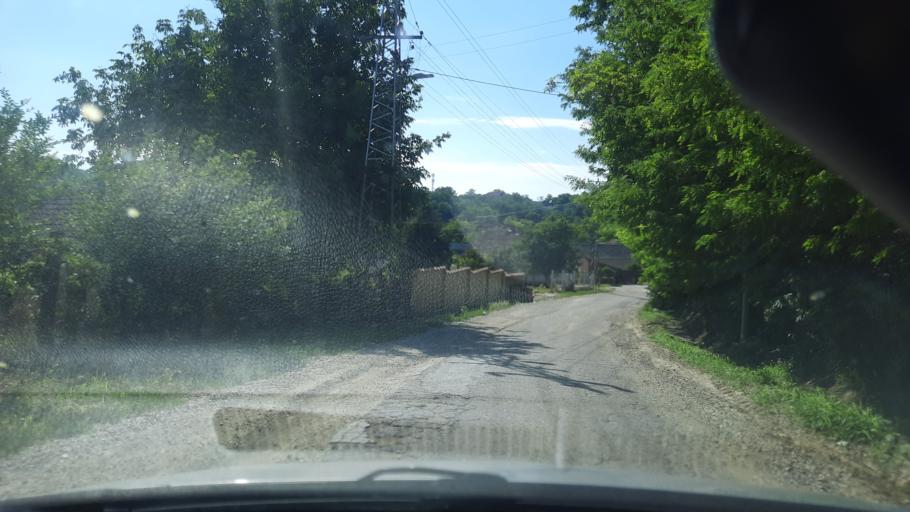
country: RS
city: Cortanovci
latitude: 45.1131
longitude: 19.9482
